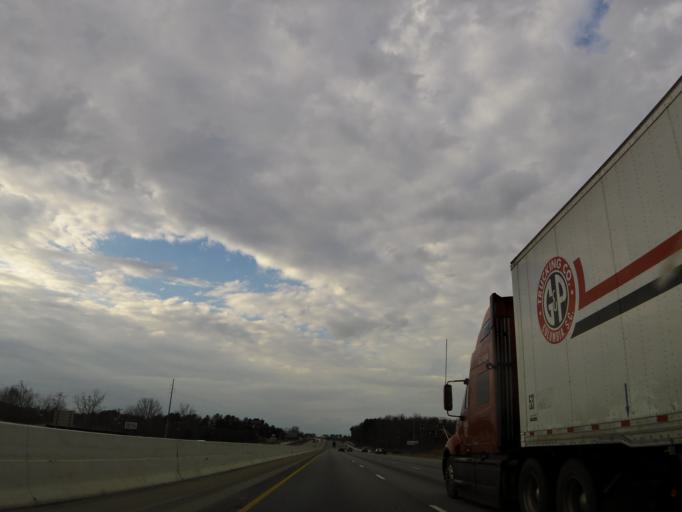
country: US
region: South Carolina
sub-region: Greenville County
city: Simpsonville
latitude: 34.7404
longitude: -82.2744
